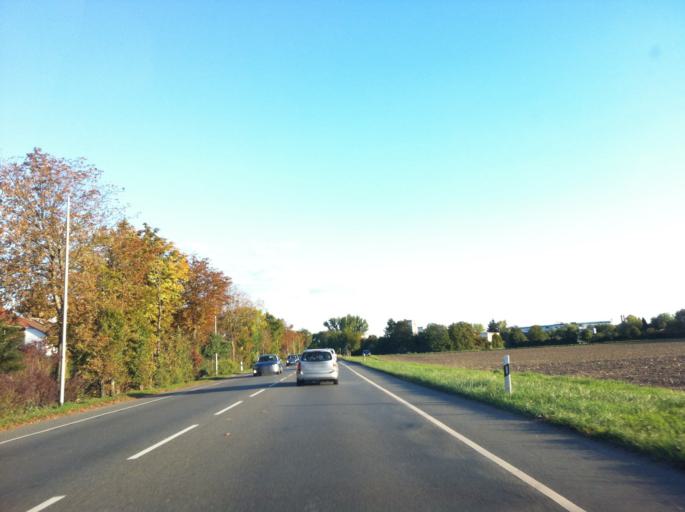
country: DE
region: Hesse
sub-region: Regierungsbezirk Darmstadt
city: Gross-Gerau
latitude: 49.9199
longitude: 8.4741
